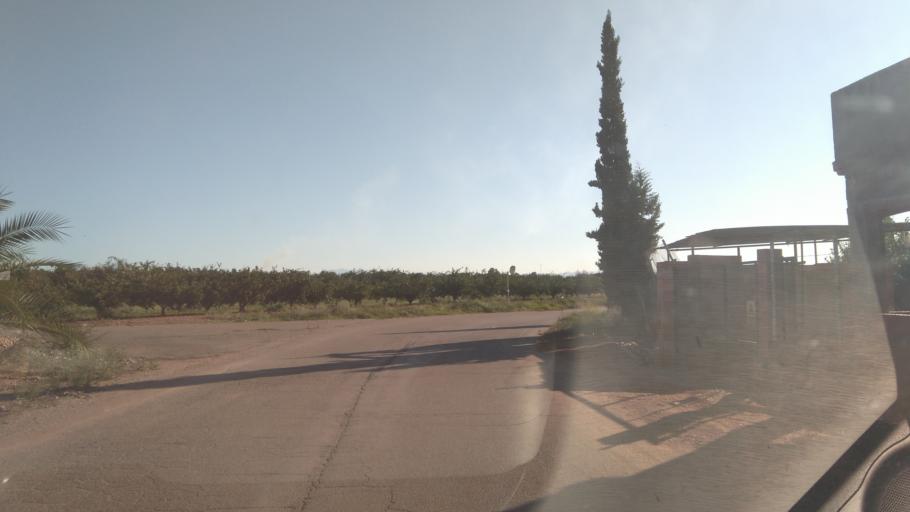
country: ES
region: Valencia
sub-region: Provincia de Valencia
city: Benimodo
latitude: 39.1799
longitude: -0.5315
